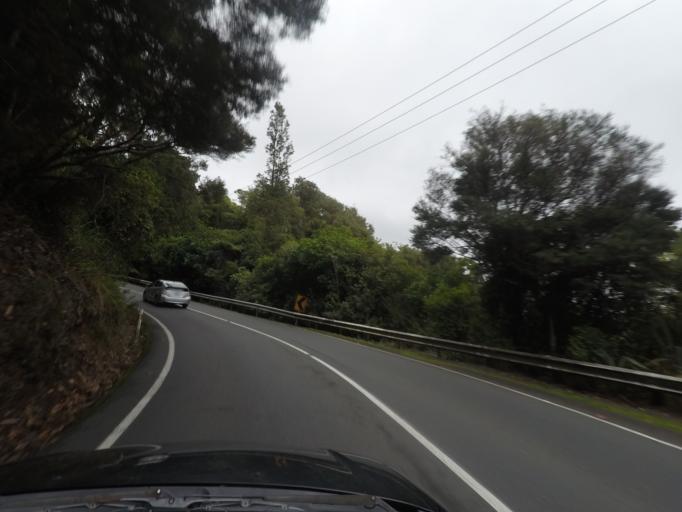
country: NZ
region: Auckland
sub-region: Auckland
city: Titirangi
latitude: -36.9332
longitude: 174.5798
